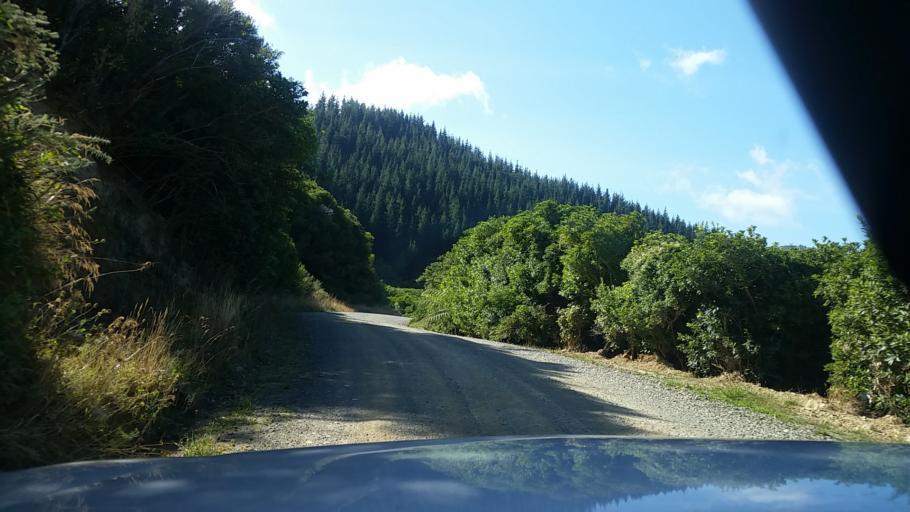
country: NZ
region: Marlborough
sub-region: Marlborough District
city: Picton
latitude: -41.2881
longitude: 174.1637
